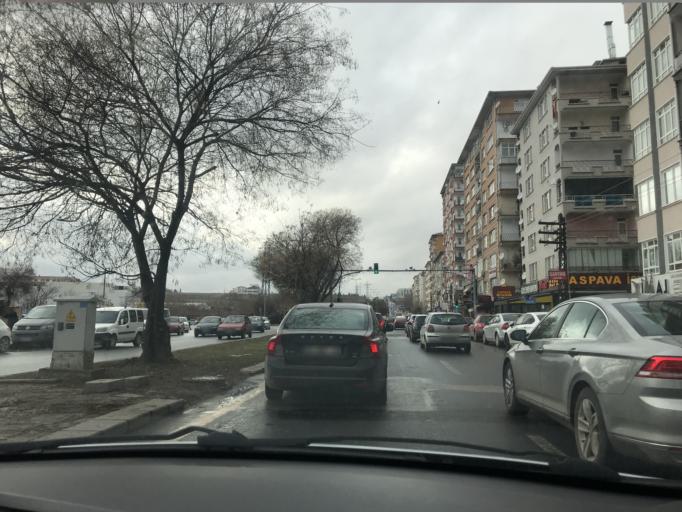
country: TR
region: Ankara
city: Batikent
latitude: 39.9579
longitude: 32.7916
